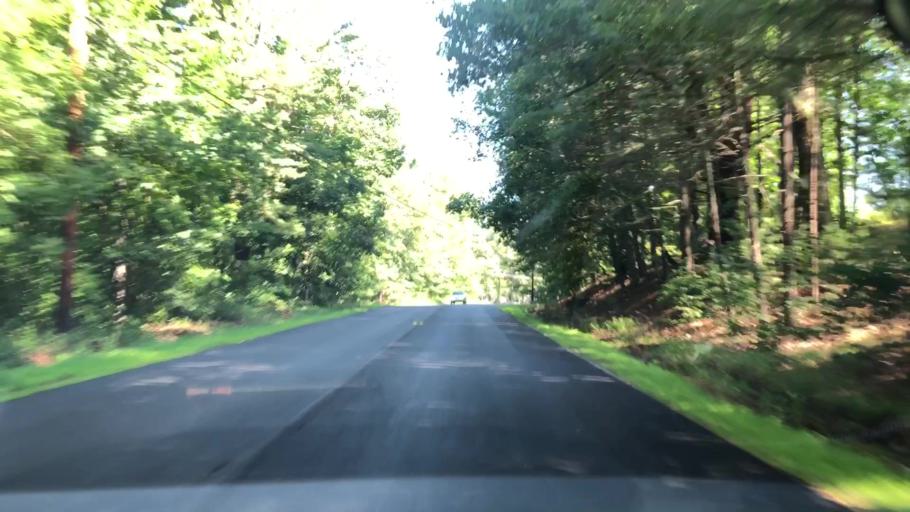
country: US
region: New Hampshire
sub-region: Hillsborough County
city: Milford
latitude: 42.8343
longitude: -71.6131
